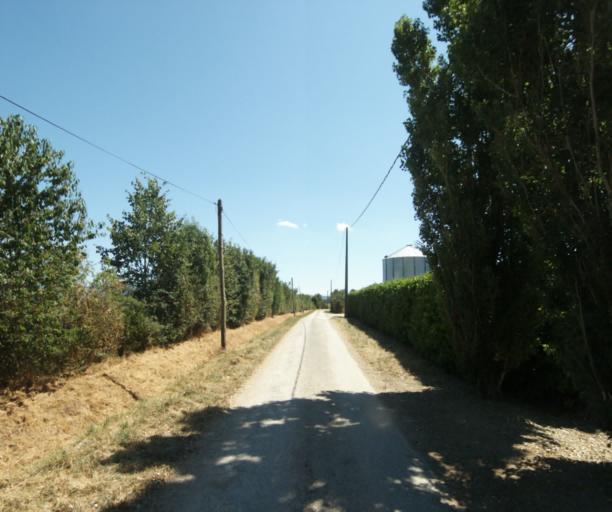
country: FR
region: Midi-Pyrenees
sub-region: Departement de la Haute-Garonne
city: Saint-Felix-Lauragais
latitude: 43.4717
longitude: 1.9414
